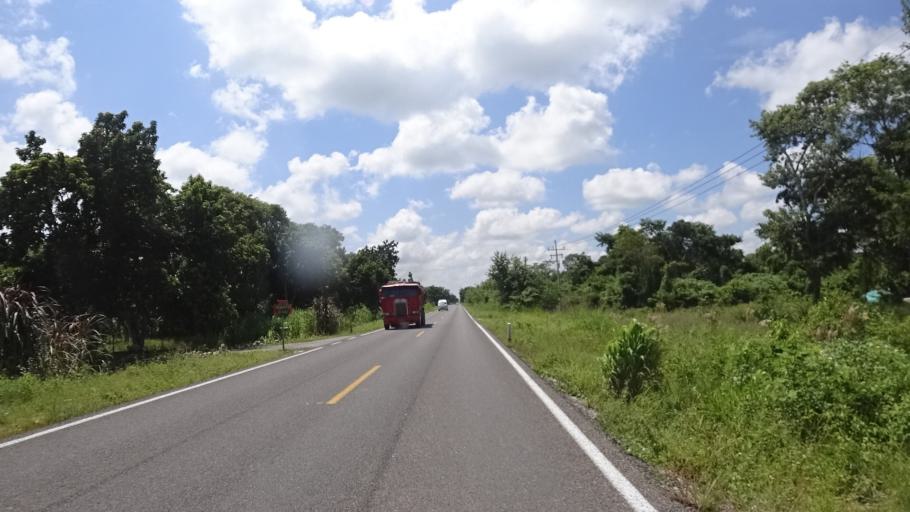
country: MX
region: Campeche
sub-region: Carmen
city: Licenciado Gustavo Diaz Ordaz (18 de Marzo)
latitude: 18.6906
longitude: -90.9758
